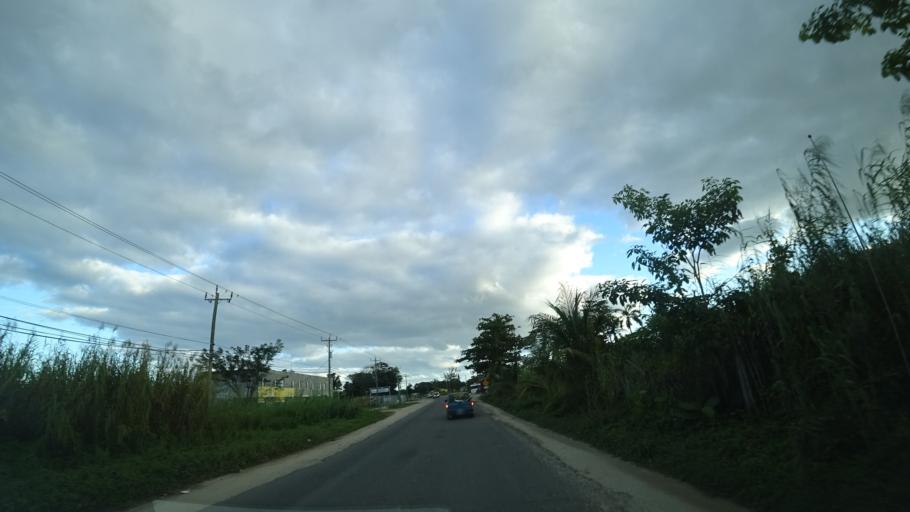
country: BZ
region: Belize
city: Belize City
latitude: 17.5523
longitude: -88.3062
